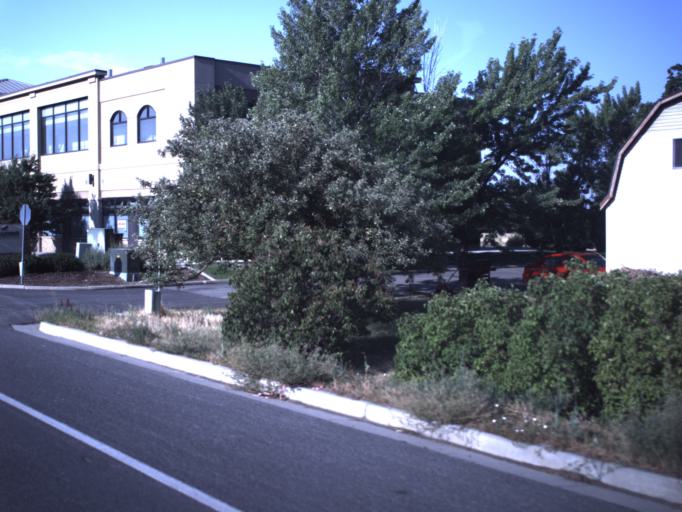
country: US
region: Utah
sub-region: Utah County
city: Alpine
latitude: 40.4344
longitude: -111.7850
